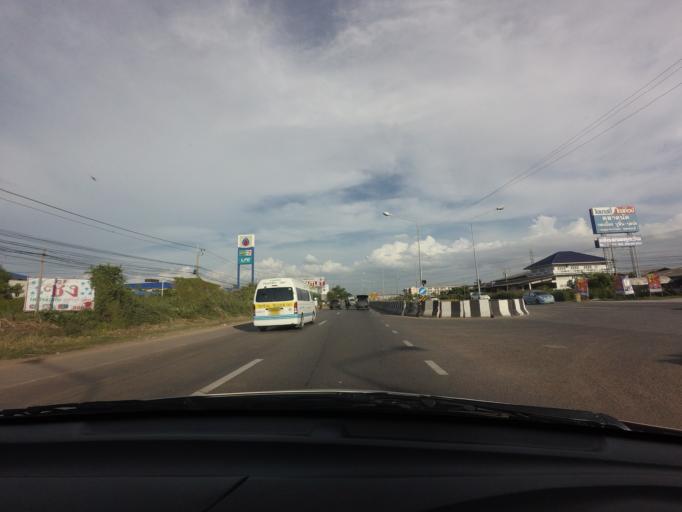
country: TH
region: Nonthaburi
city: Bang Bua Thong
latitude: 13.9710
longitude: 100.3954
